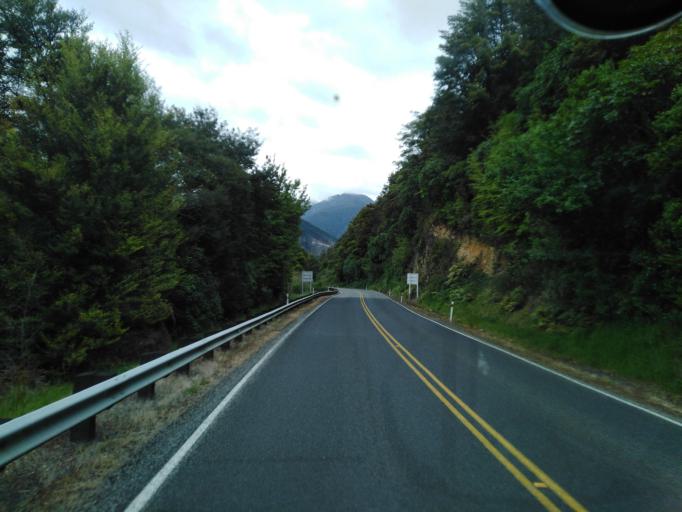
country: NZ
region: Tasman
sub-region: Tasman District
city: Wakefield
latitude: -41.7056
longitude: 172.5863
